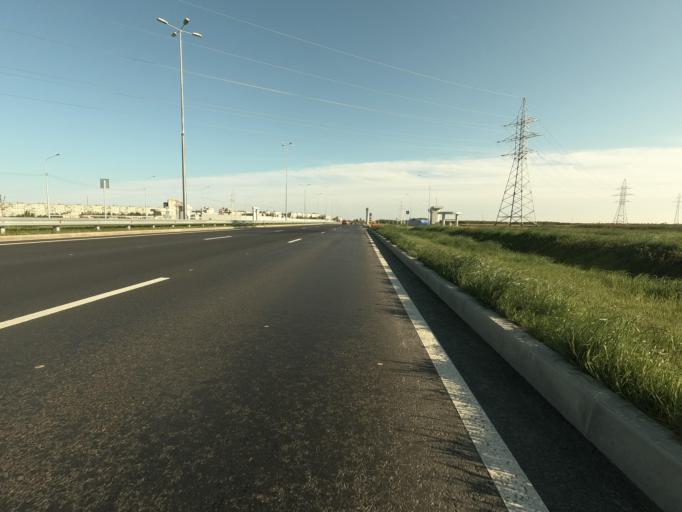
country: RU
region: St.-Petersburg
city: Kolpino
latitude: 59.7405
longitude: 30.5474
